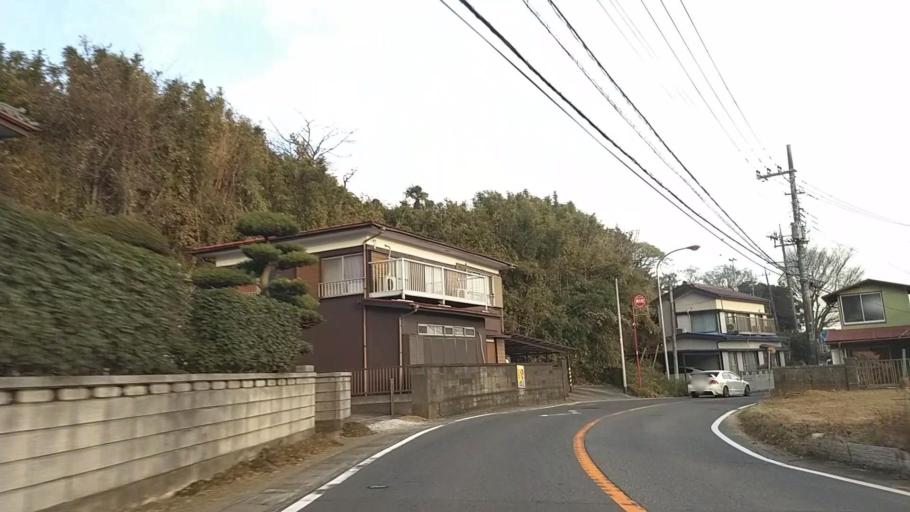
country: JP
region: Kanagawa
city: Atsugi
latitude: 35.4349
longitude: 139.3222
